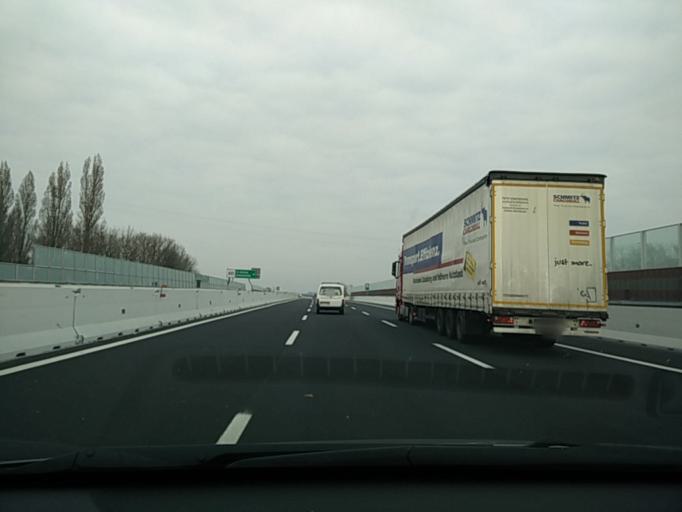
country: IT
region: Veneto
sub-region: Provincia di Venezia
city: Meolo
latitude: 45.6316
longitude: 12.4477
